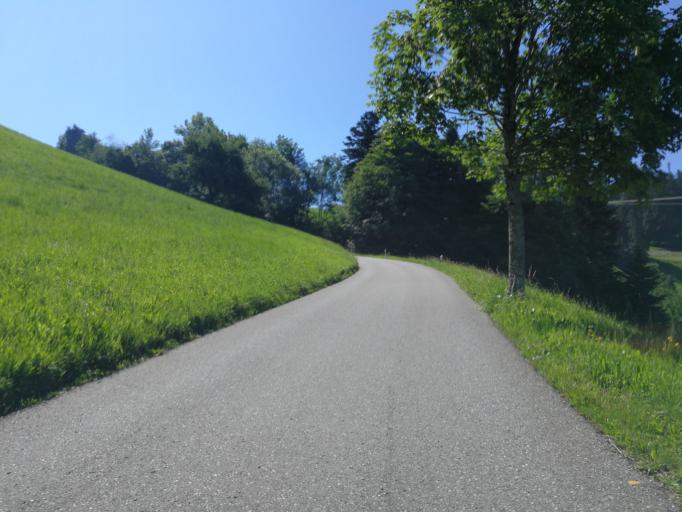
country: CH
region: Zurich
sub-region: Bezirk Hinwil
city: Hadlikon
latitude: 47.2912
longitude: 8.8803
